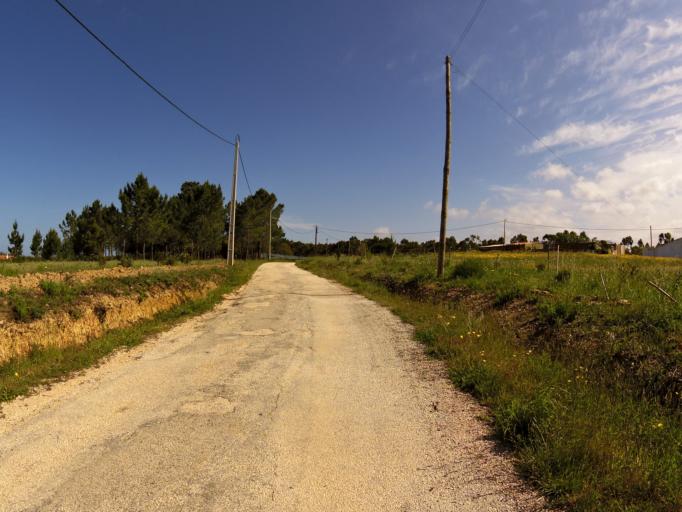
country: PT
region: Faro
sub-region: Aljezur
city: Aljezur
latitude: 37.3365
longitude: -8.8084
